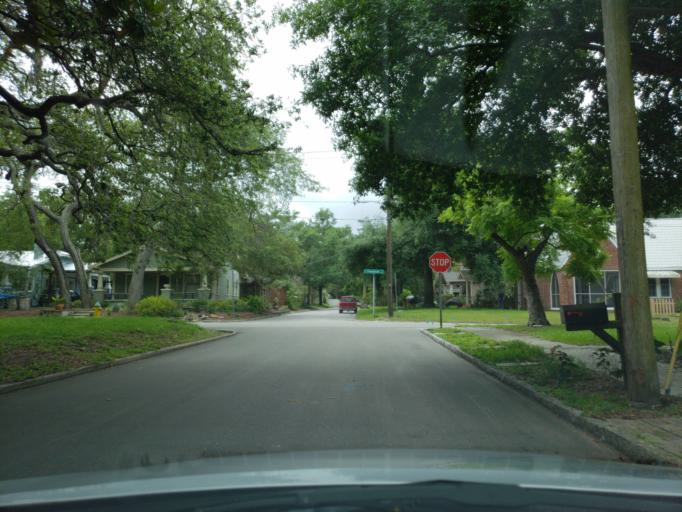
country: US
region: Florida
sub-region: Hillsborough County
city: Tampa
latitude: 27.9990
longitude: -82.4503
